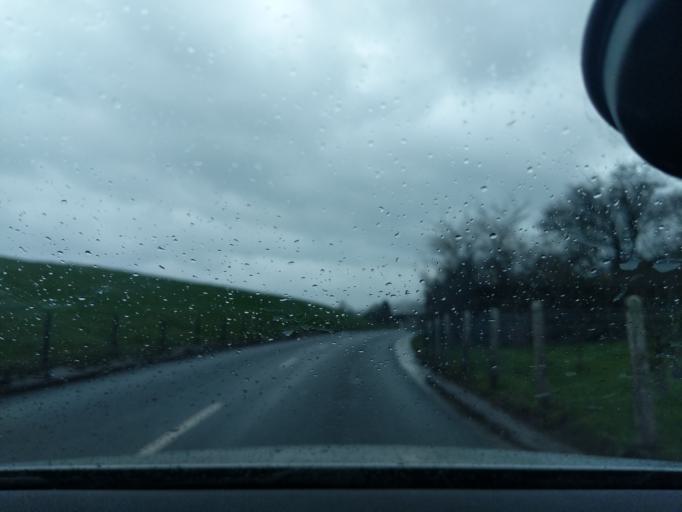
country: DE
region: Lower Saxony
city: Grunendeich
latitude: 53.5790
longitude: 9.6087
